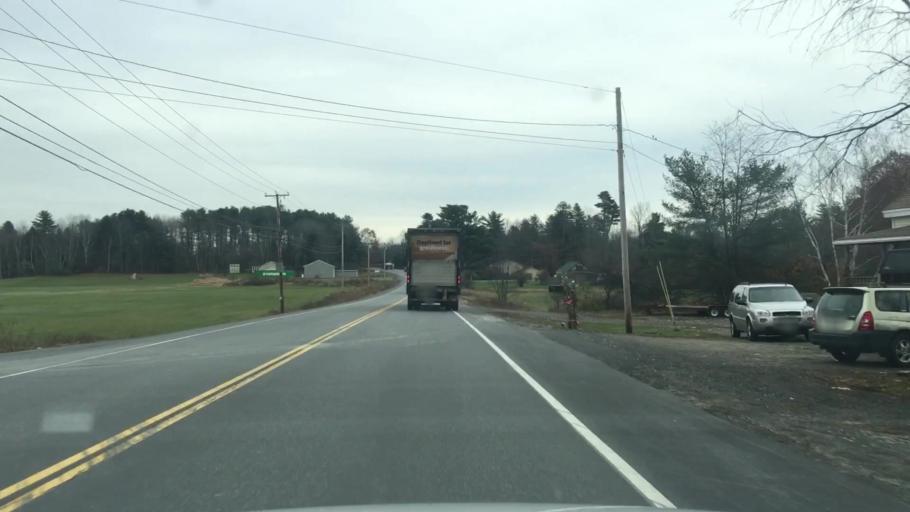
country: US
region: Maine
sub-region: Waldo County
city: Belfast
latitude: 44.4142
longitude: -69.0539
